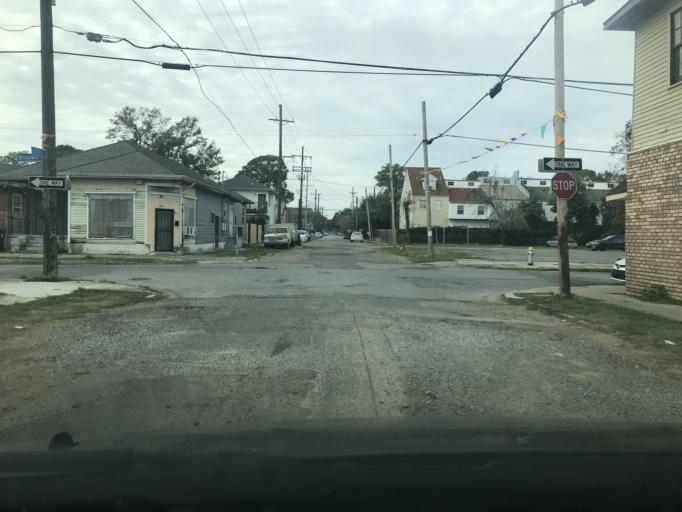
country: US
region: Louisiana
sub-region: Orleans Parish
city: New Orleans
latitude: 29.9567
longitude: -90.1115
